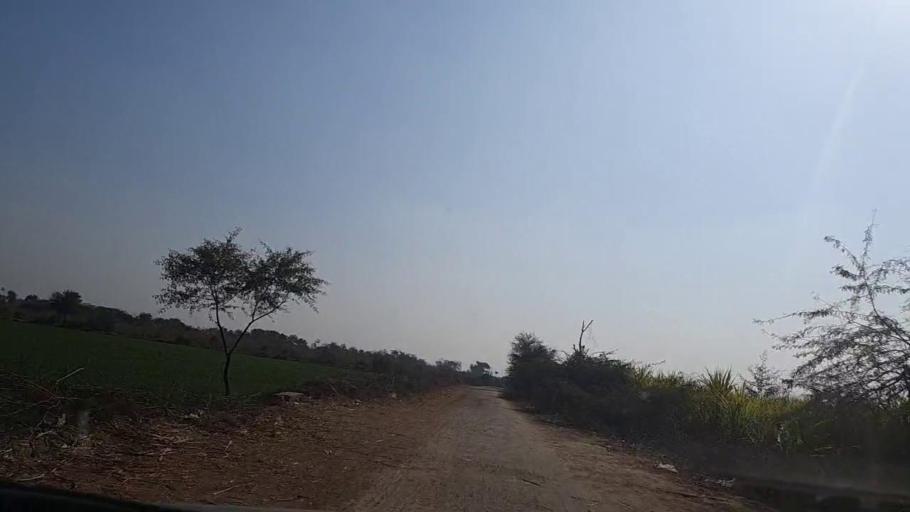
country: PK
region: Sindh
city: Sakrand
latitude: 26.0741
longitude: 68.3695
